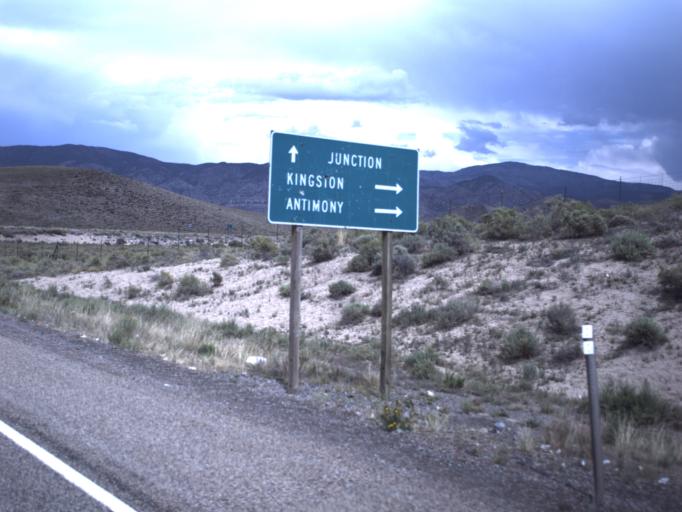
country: US
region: Utah
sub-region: Piute County
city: Junction
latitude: 38.2083
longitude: -112.2254
